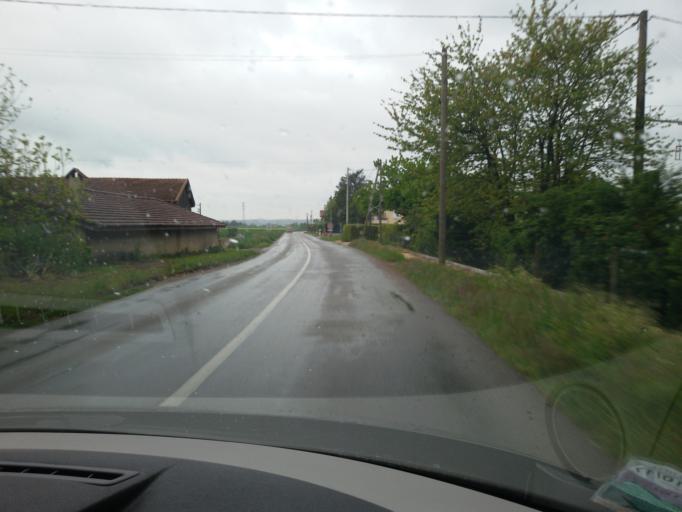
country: FR
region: Rhone-Alpes
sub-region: Departement de la Drome
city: Bourg-de-Peage
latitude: 45.0171
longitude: 5.0805
